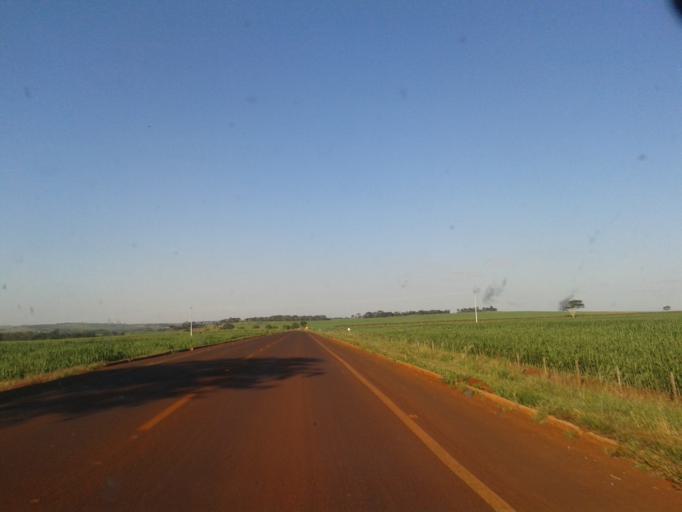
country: BR
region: Minas Gerais
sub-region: Capinopolis
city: Capinopolis
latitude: -18.6983
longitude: -49.6408
